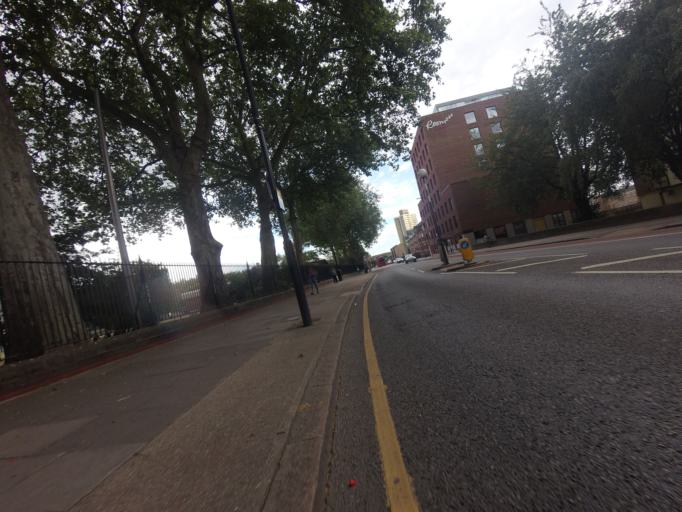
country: GB
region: England
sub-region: Greater London
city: Poplar
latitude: 51.5382
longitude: 0.0056
